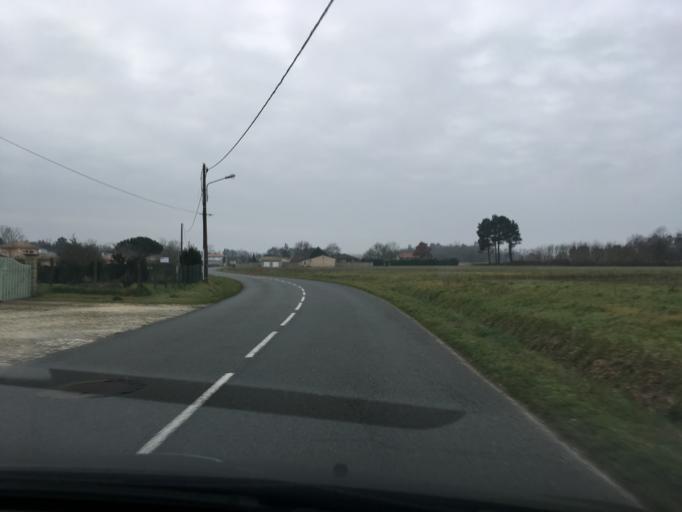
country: FR
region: Aquitaine
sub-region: Departement de la Gironde
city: Saint-Ciers-sur-Gironde
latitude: 45.2837
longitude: -0.6019
